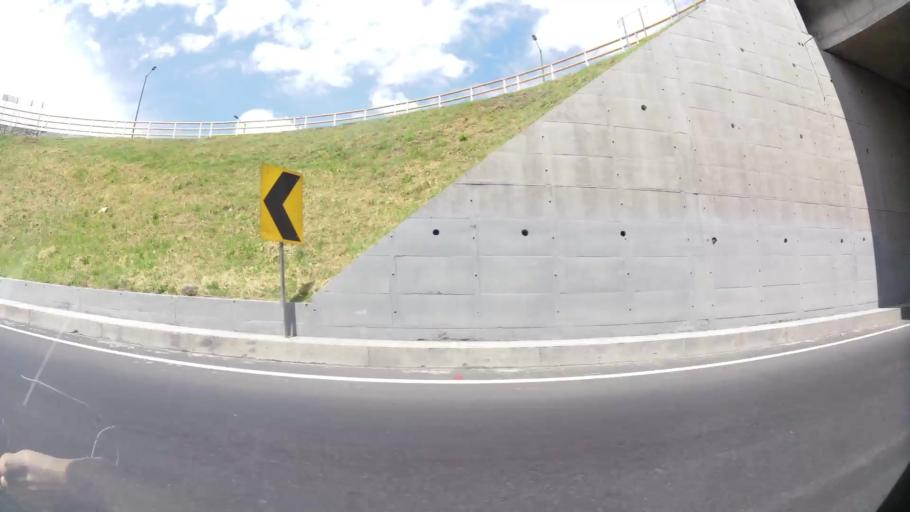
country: EC
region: Pichincha
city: Sangolqui
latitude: -0.2251
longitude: -78.3478
